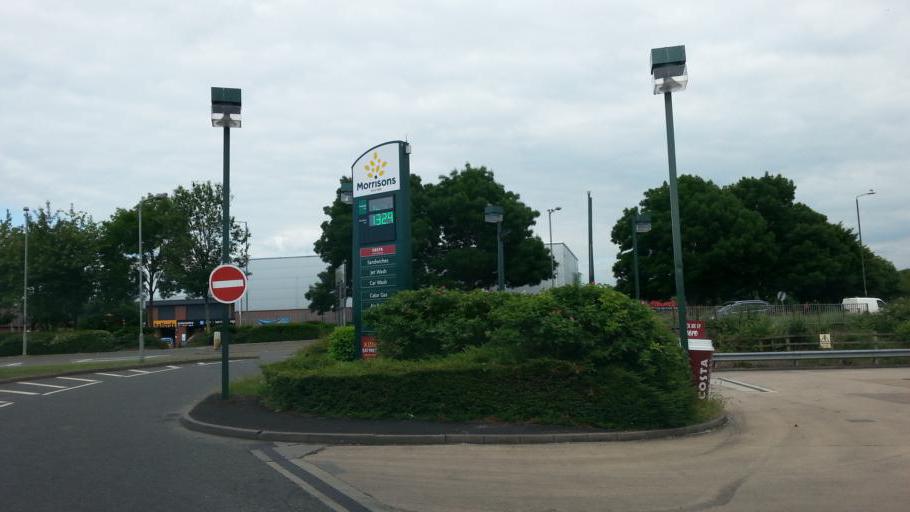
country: GB
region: England
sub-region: Worcestershire
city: Evesham
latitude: 52.0772
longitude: -1.9382
